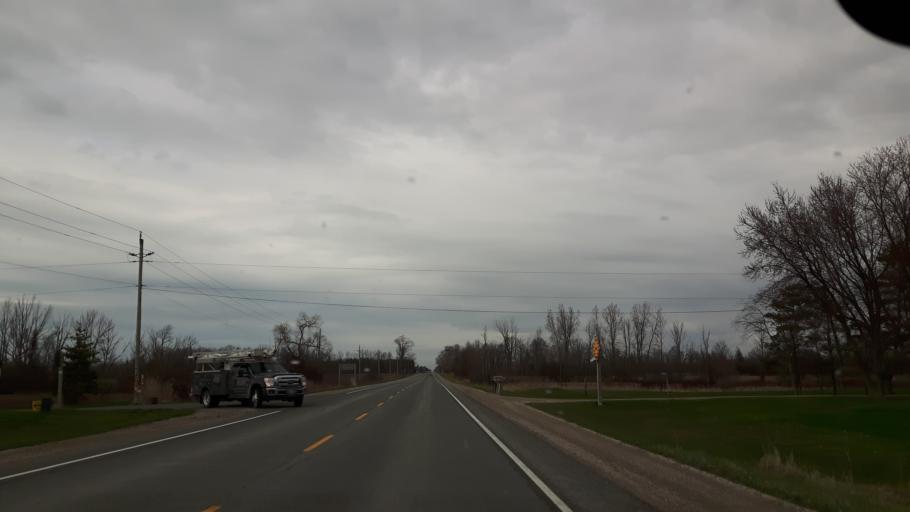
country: CA
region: Ontario
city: Goderich
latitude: 43.5928
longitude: -81.7056
